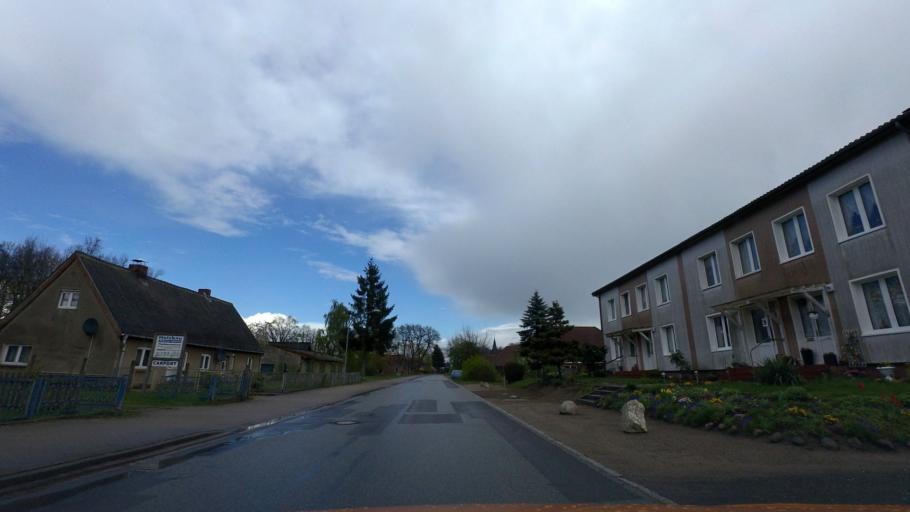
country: DE
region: Mecklenburg-Vorpommern
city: Nostorf
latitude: 53.4053
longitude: 10.6497
